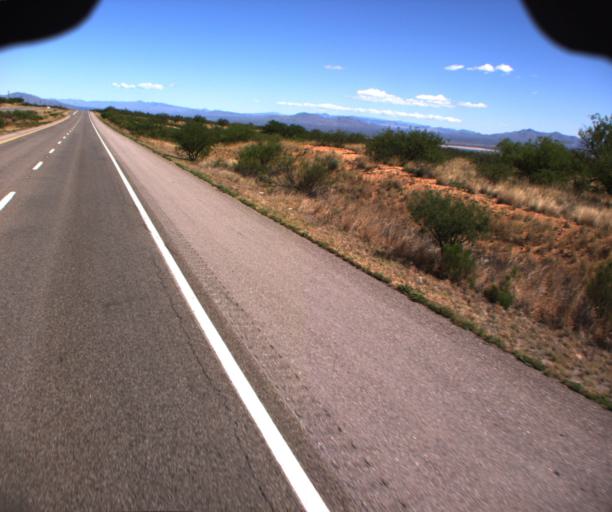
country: US
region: Arizona
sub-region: Cochise County
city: Whetstone
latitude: 31.8774
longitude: -110.3410
